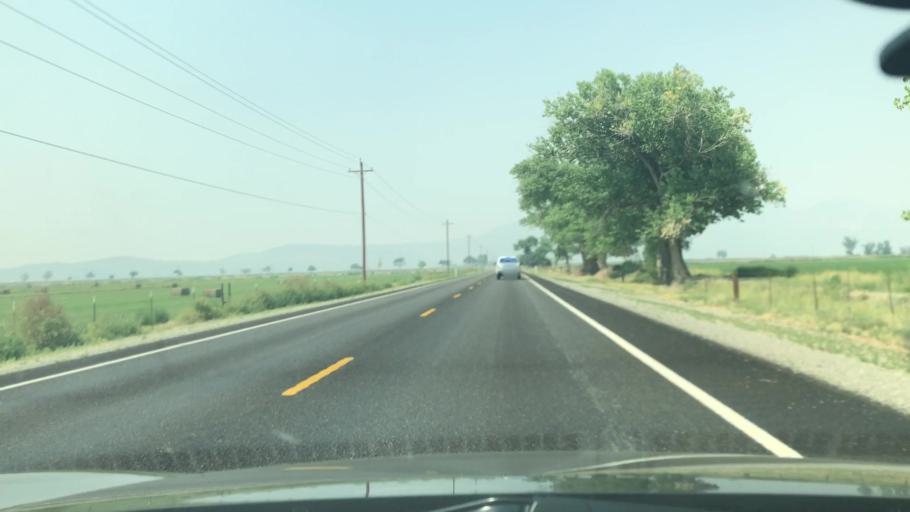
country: US
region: Nevada
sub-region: Lyon County
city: Yerington
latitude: 39.1212
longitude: -119.1810
